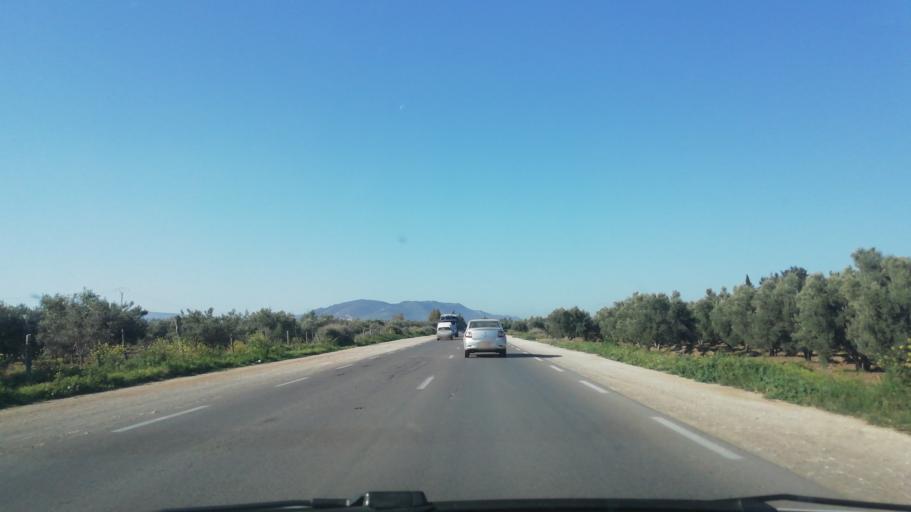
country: DZ
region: Mascara
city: Sig
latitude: 35.5517
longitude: -0.1112
